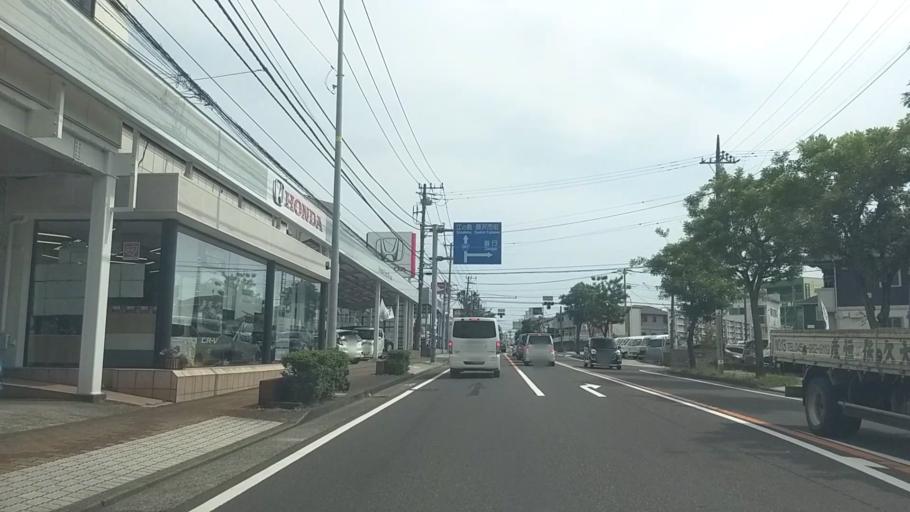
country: JP
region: Kanagawa
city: Fujisawa
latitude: 35.3655
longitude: 139.4790
